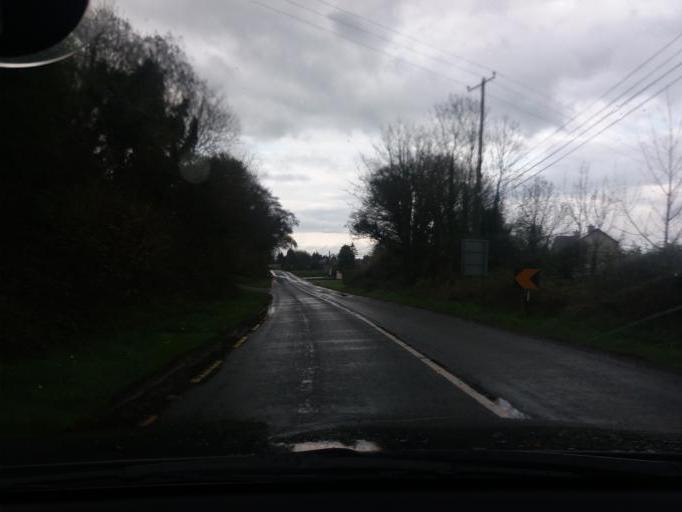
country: IE
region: Ulster
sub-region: An Cabhan
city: Ballyconnell
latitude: 54.1167
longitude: -7.6640
